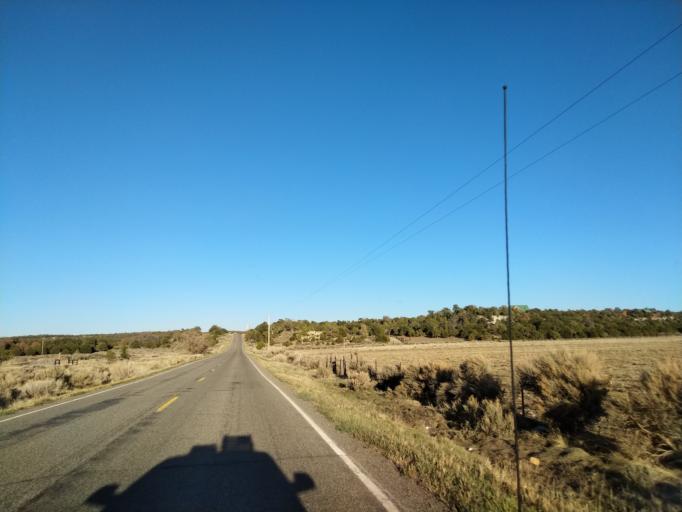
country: US
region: Colorado
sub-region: Mesa County
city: Redlands
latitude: 38.9938
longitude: -108.7337
